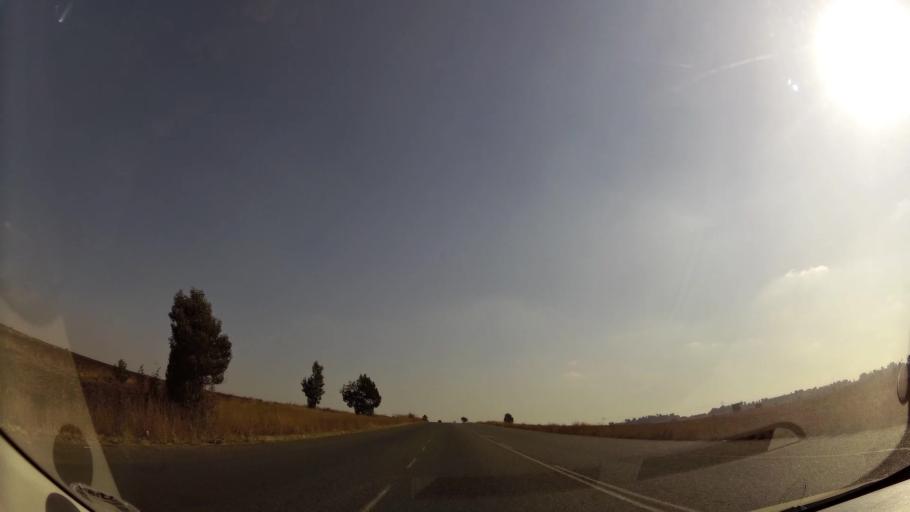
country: ZA
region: Gauteng
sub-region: West Rand District Municipality
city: Randfontein
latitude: -26.1822
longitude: 27.7442
